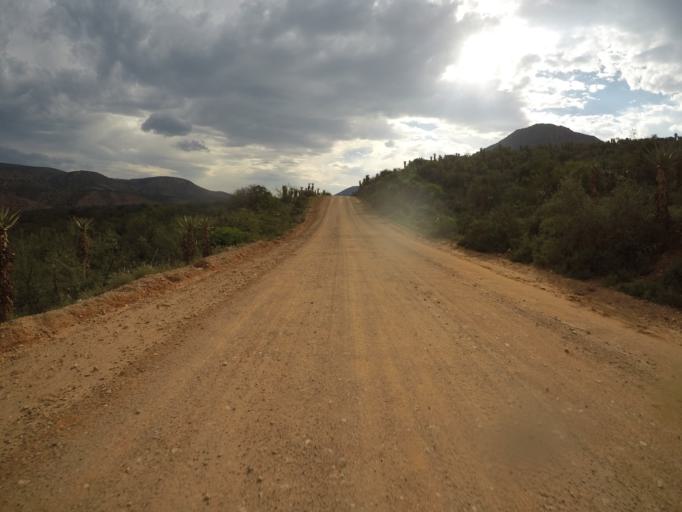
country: ZA
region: Eastern Cape
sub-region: Cacadu District Municipality
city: Kareedouw
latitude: -33.5827
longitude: 24.1612
